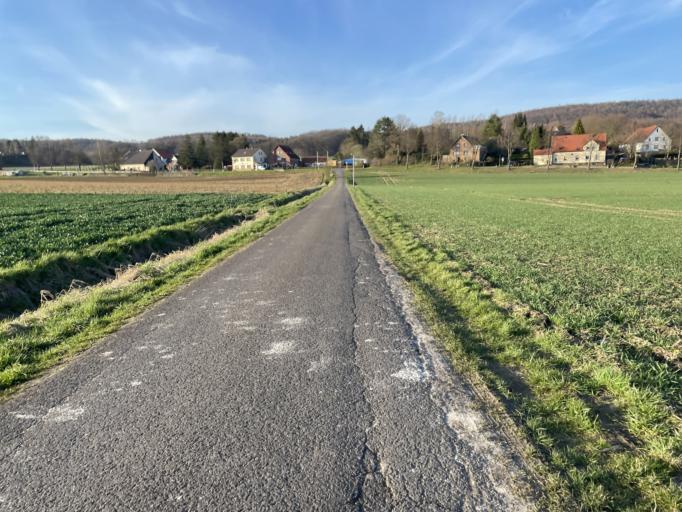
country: DE
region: North Rhine-Westphalia
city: Porta Westfalica
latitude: 52.2266
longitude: 8.9544
